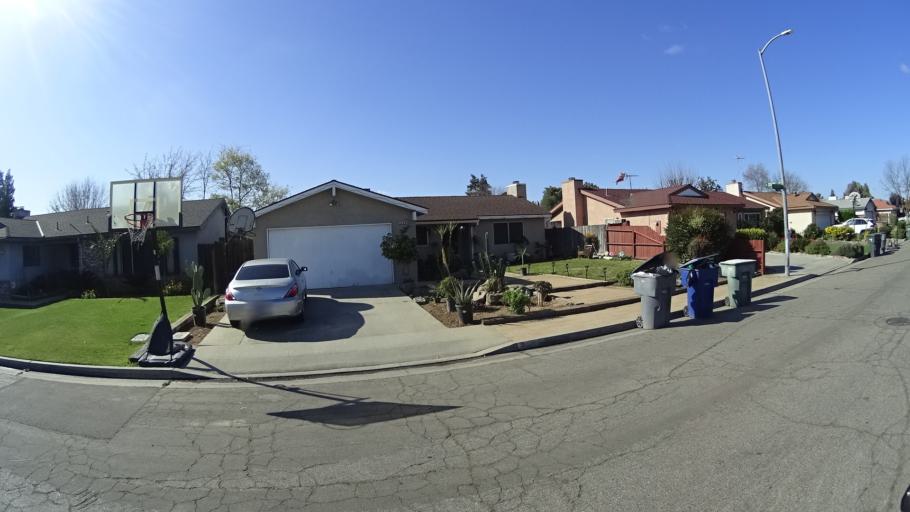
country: US
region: California
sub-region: Fresno County
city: West Park
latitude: 36.7982
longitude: -119.8862
